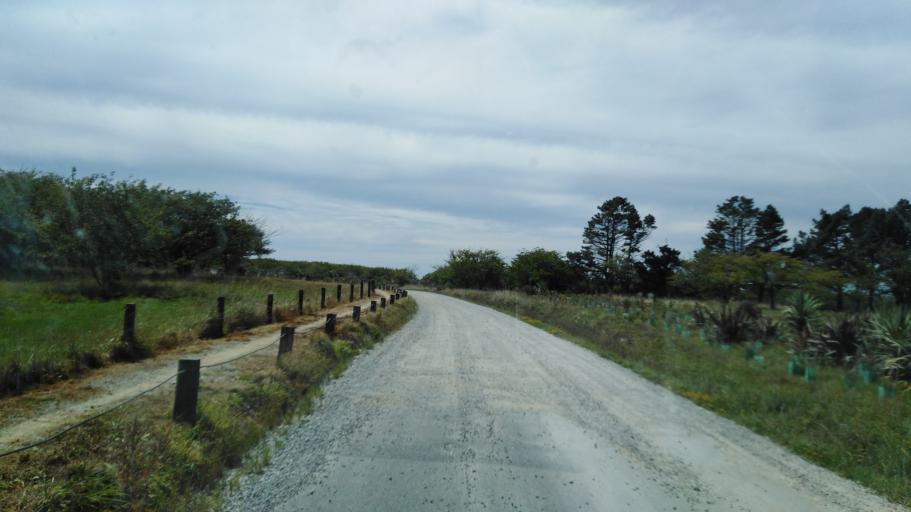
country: NZ
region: West Coast
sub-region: Buller District
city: Westport
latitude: -41.7383
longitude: 171.6042
